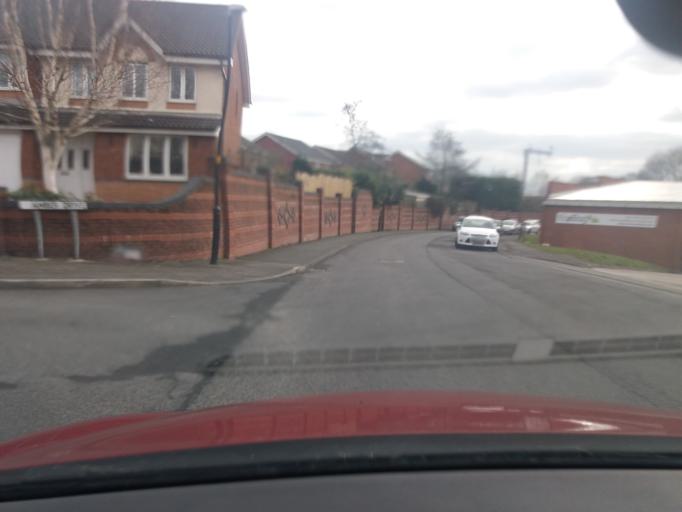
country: GB
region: England
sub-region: Lancashire
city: Chorley
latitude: 53.6455
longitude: -2.6172
